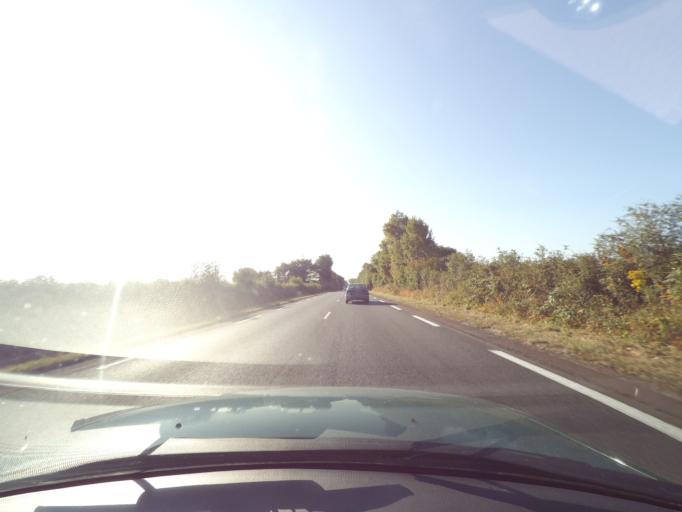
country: FR
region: Poitou-Charentes
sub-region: Departement des Deux-Sevres
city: Chiche
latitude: 46.8179
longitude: -0.4036
